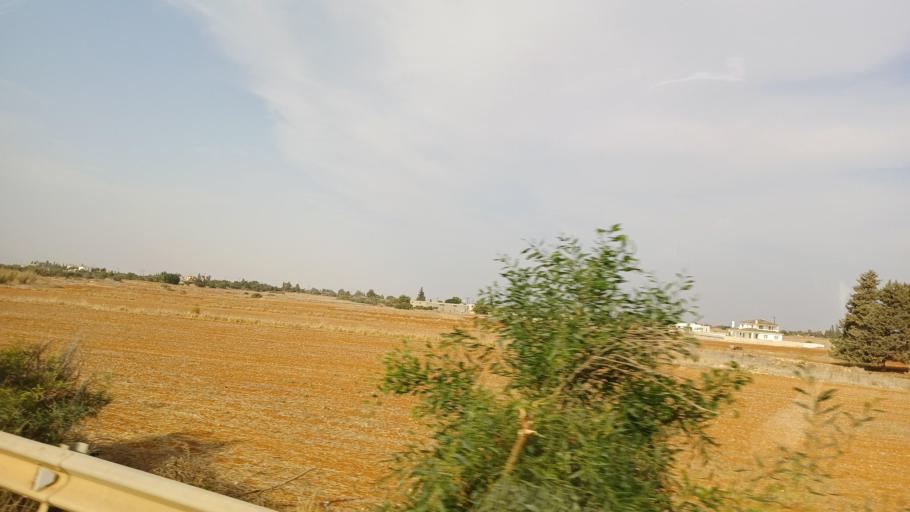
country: CY
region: Ammochostos
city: Frenaros
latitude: 35.0469
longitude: 33.9168
